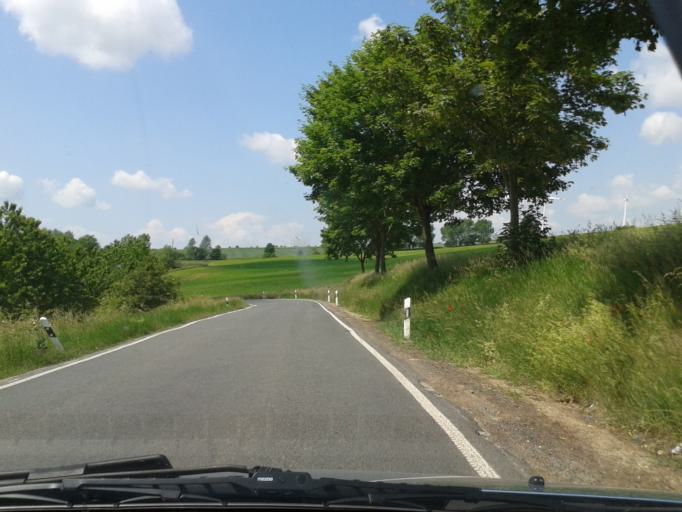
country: DE
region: Thuringia
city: Schmiedehausen
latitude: 51.0429
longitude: 11.6540
